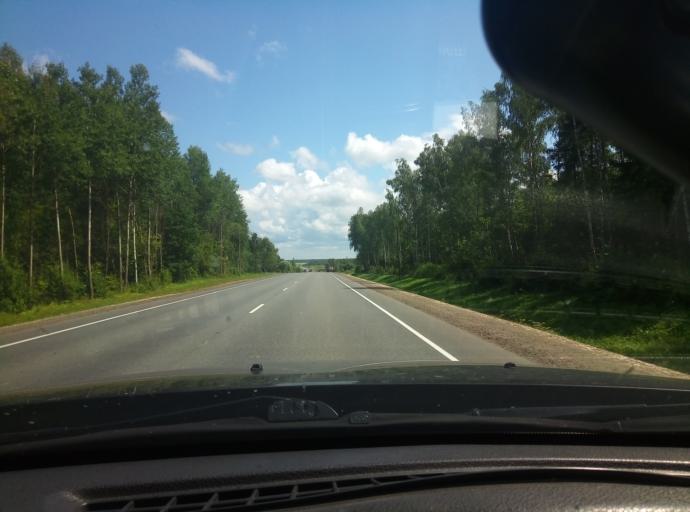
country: RU
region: Tula
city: Dubna
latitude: 54.3078
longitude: 37.0226
